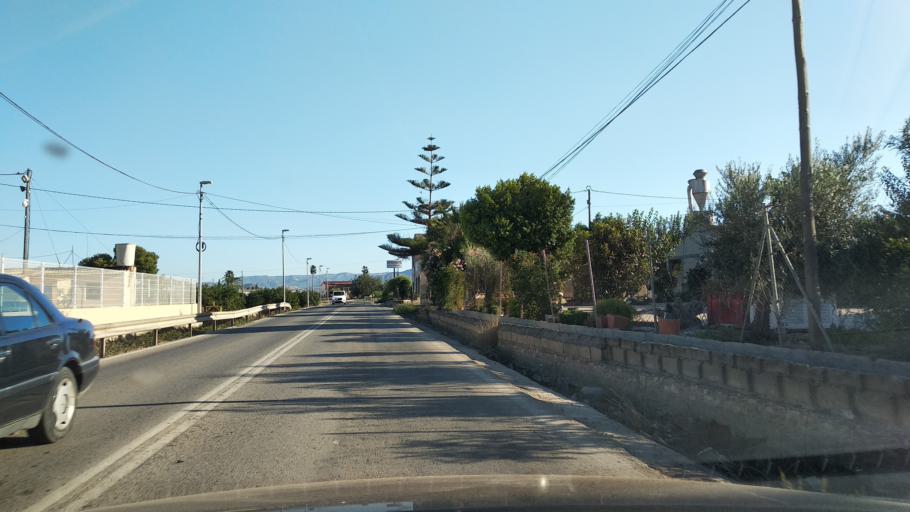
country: ES
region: Murcia
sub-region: Murcia
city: Santomera
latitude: 38.0468
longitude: -1.0542
